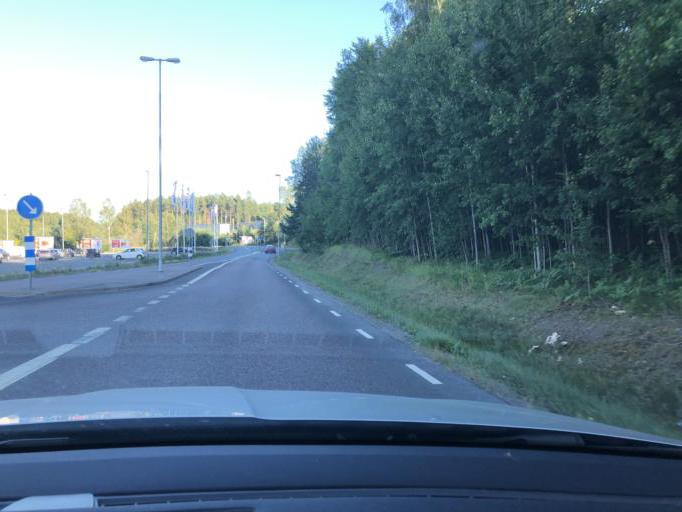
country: SE
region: Stockholm
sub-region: Sodertalje Kommun
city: Soedertaelje
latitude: 59.1860
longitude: 17.5809
